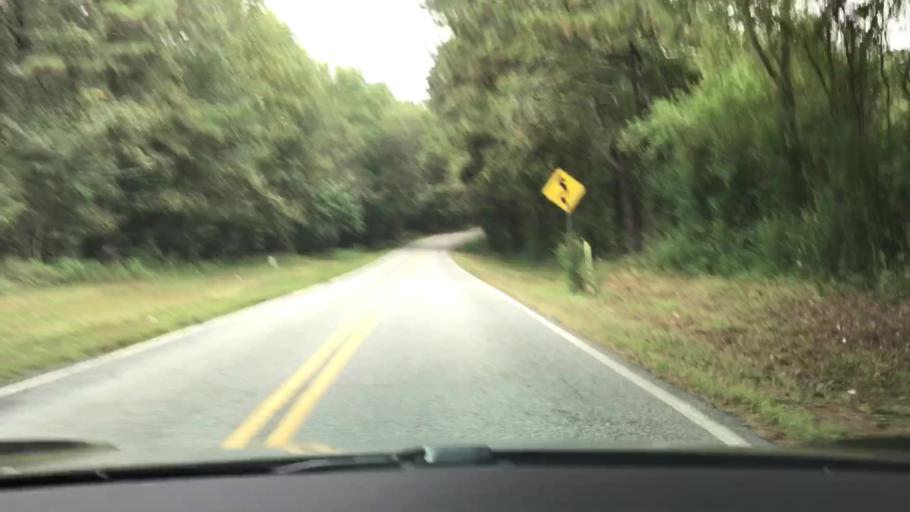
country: US
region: Georgia
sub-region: Barrow County
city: Auburn
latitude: 34.0337
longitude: -83.7984
